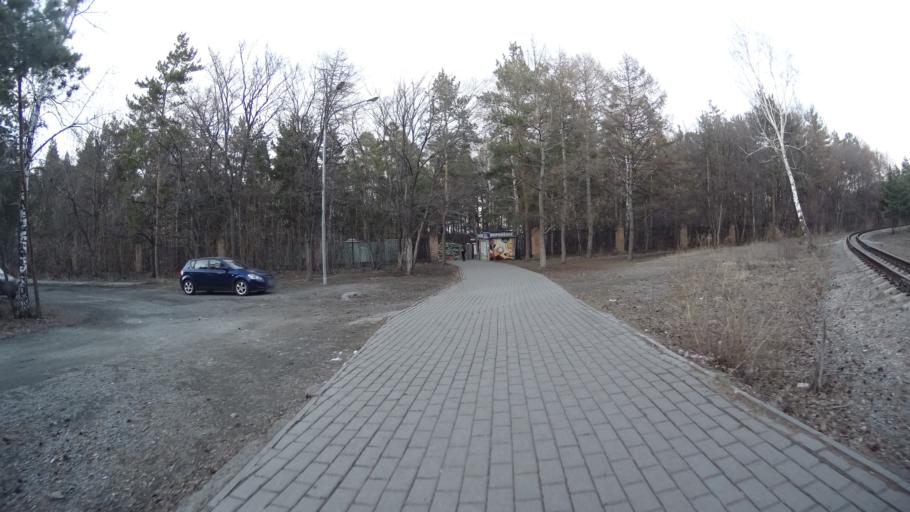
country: RU
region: Chelyabinsk
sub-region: Gorod Chelyabinsk
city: Chelyabinsk
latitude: 55.1656
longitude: 61.3704
